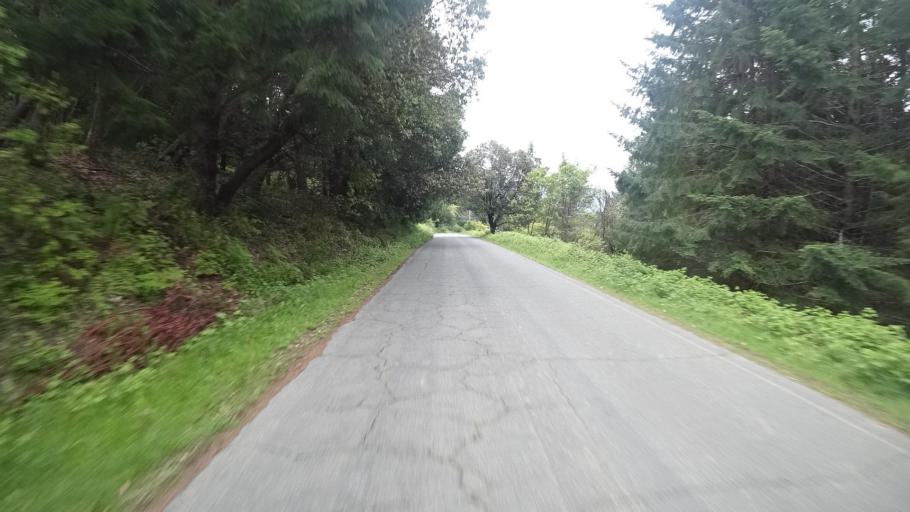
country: US
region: California
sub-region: Humboldt County
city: Willow Creek
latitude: 41.1148
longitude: -123.7178
